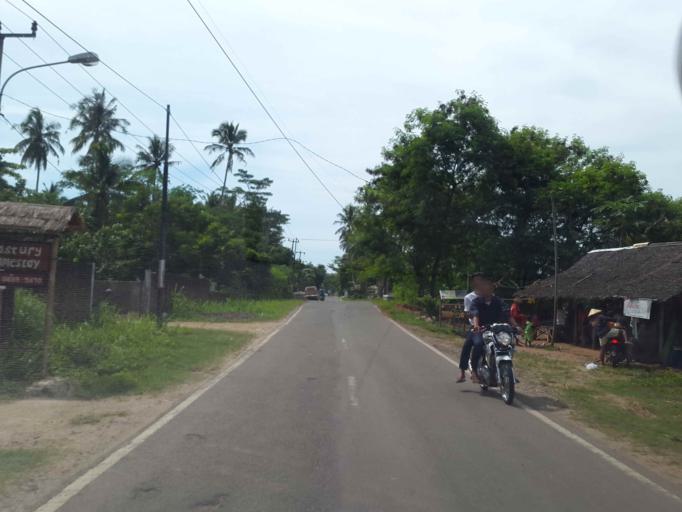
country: ID
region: Banten
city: Citeureup
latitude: -6.5249
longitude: 105.6949
